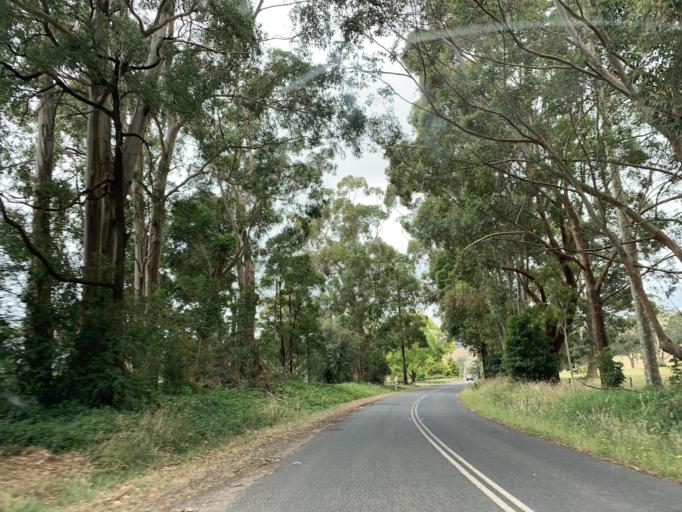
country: AU
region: Victoria
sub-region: Baw Baw
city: Warragul
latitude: -38.2439
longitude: 146.0011
